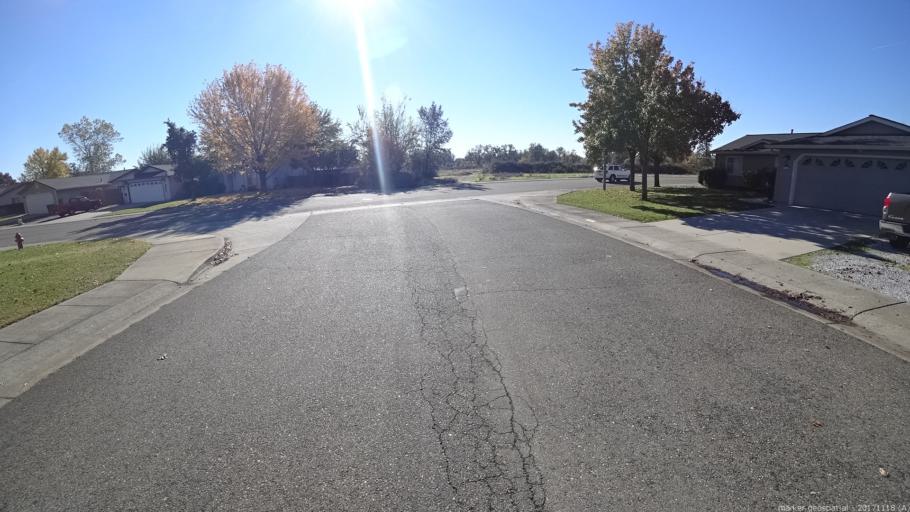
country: US
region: California
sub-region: Shasta County
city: Cottonwood
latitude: 40.3917
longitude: -122.2794
